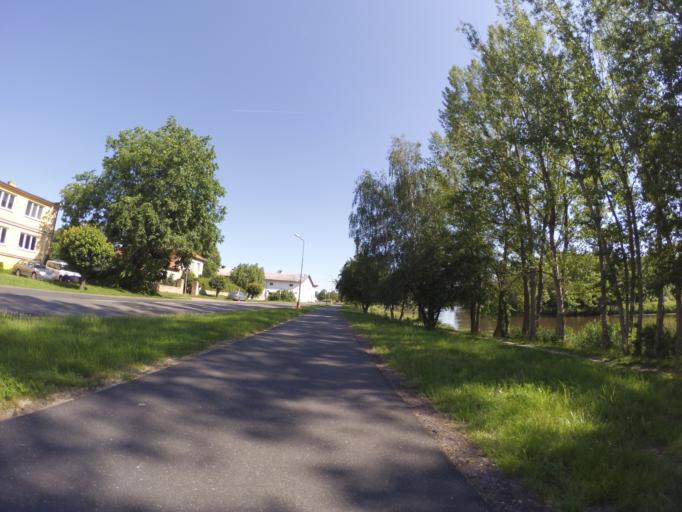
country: CZ
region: Central Bohemia
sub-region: Okres Nymburk
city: Podebrady
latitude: 50.1581
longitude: 15.1055
